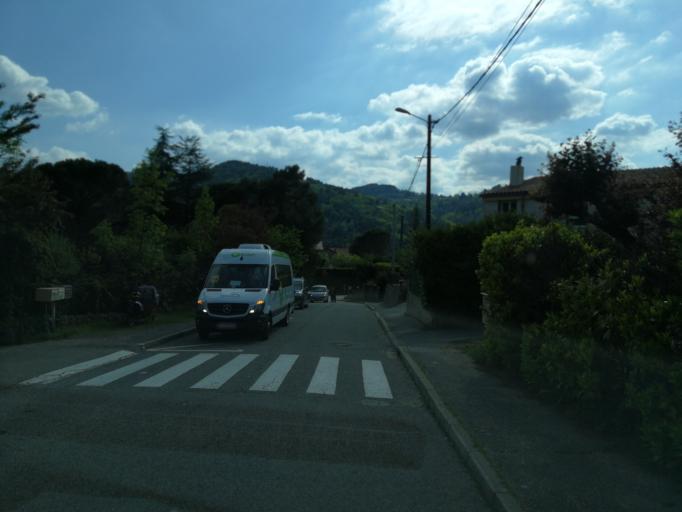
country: FR
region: Rhone-Alpes
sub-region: Departement de l'Ardeche
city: Saint-Sauveur-de-Montagut
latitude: 44.8054
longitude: 4.6219
